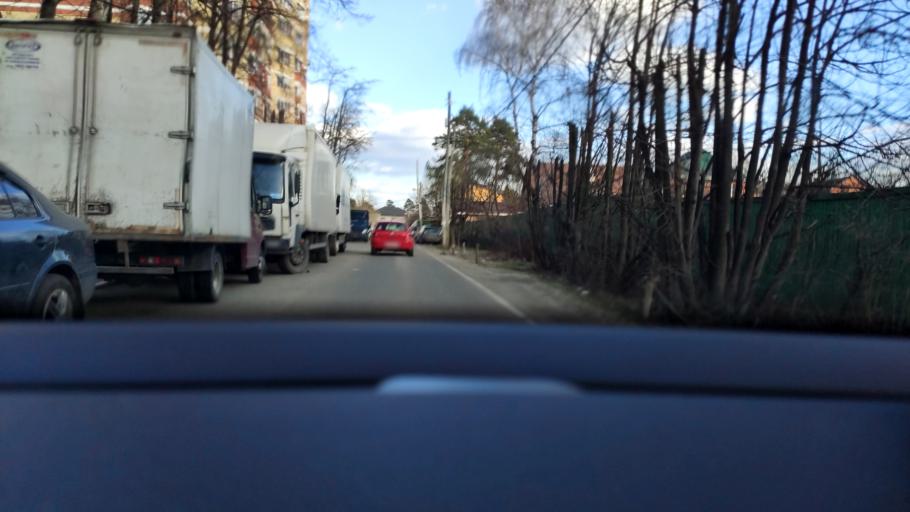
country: RU
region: Moskovskaya
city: Reutov
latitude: 55.7751
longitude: 37.8953
